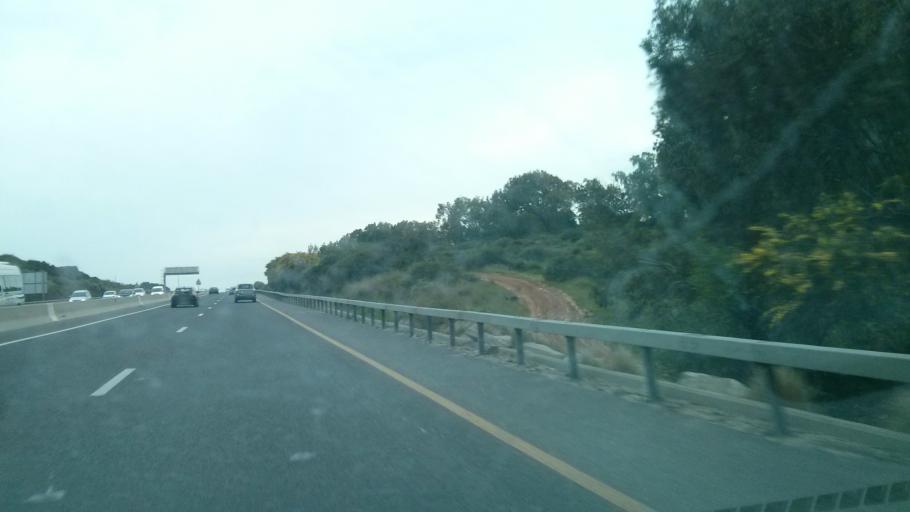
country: IL
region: Haifa
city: Hadera
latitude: 32.4654
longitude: 34.8966
